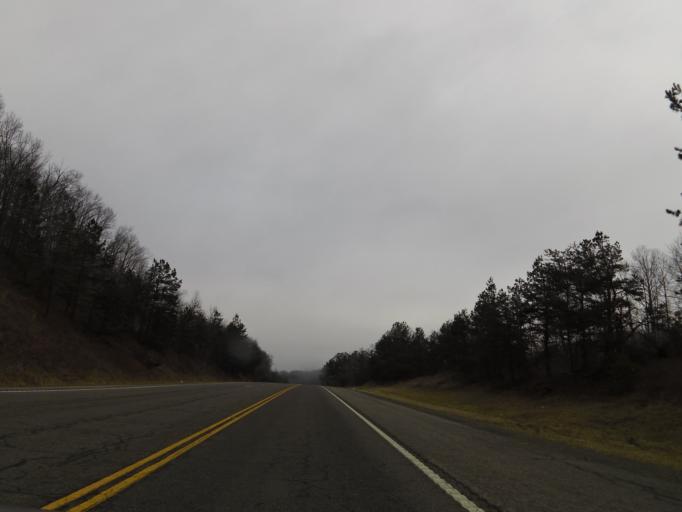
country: US
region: Tennessee
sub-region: Morgan County
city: Wartburg
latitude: 36.2210
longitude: -84.6670
